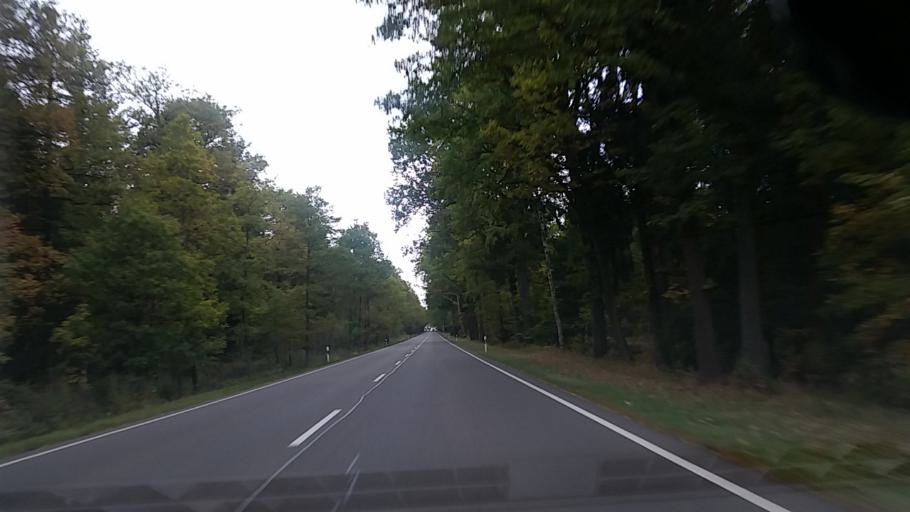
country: DE
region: Lower Saxony
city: Sprakensehl
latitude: 52.8249
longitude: 10.4895
